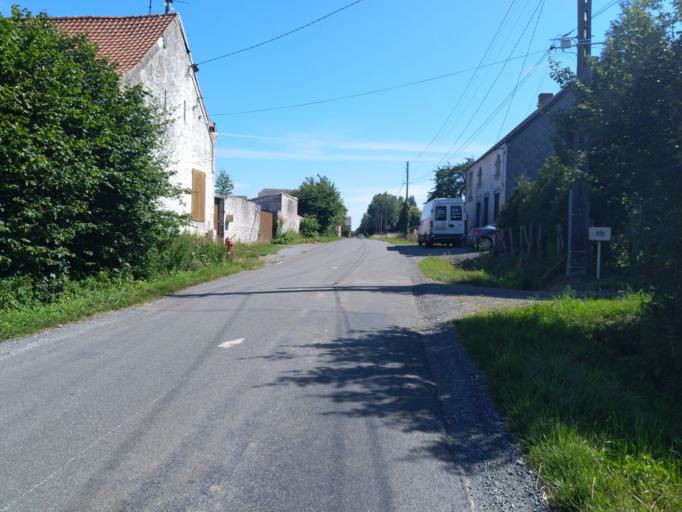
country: FR
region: Nord-Pas-de-Calais
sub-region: Departement du Nord
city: La Longueville
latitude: 50.3278
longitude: 3.8305
